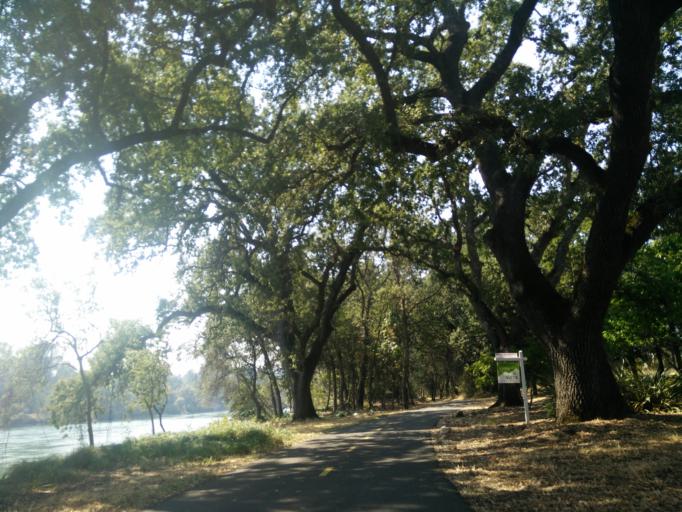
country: US
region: California
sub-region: Shasta County
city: Redding
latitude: 40.5939
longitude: -122.4064
